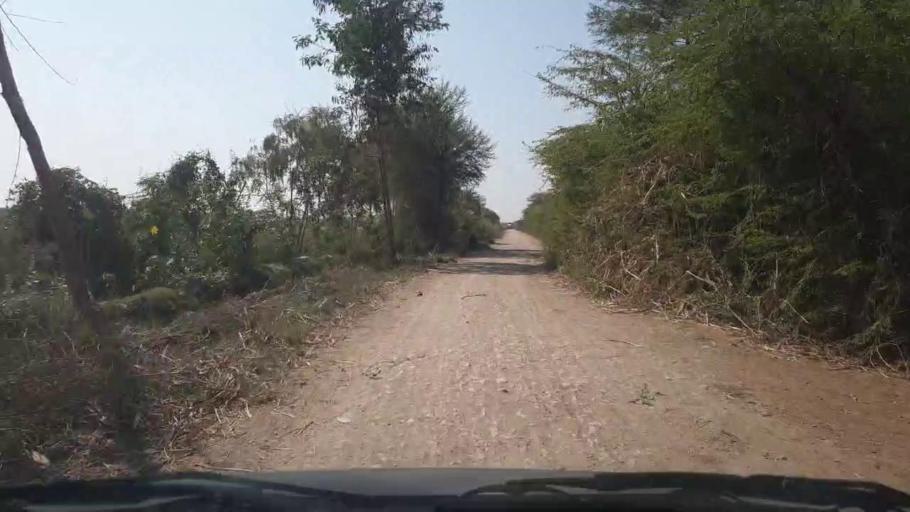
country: PK
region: Sindh
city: Samaro
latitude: 25.2692
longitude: 69.3462
